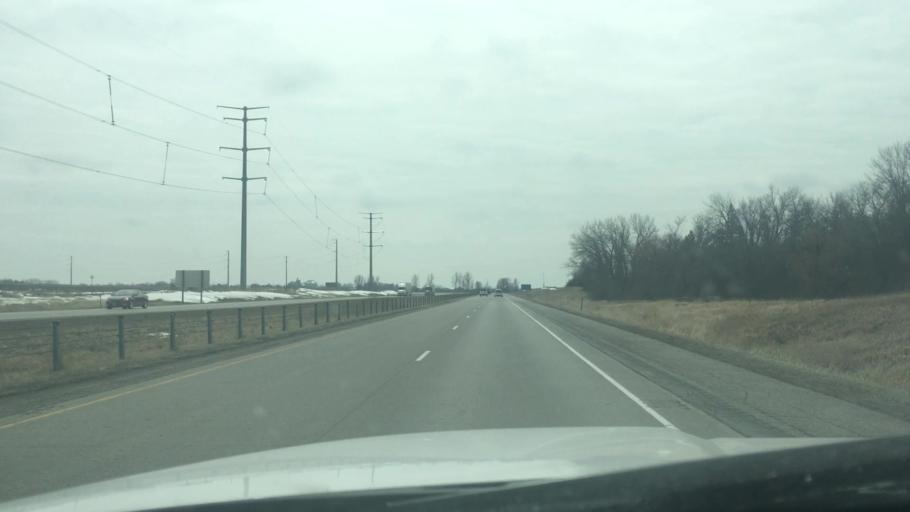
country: US
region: Minnesota
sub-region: Clay County
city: Barnesville
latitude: 46.4957
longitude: -96.2909
